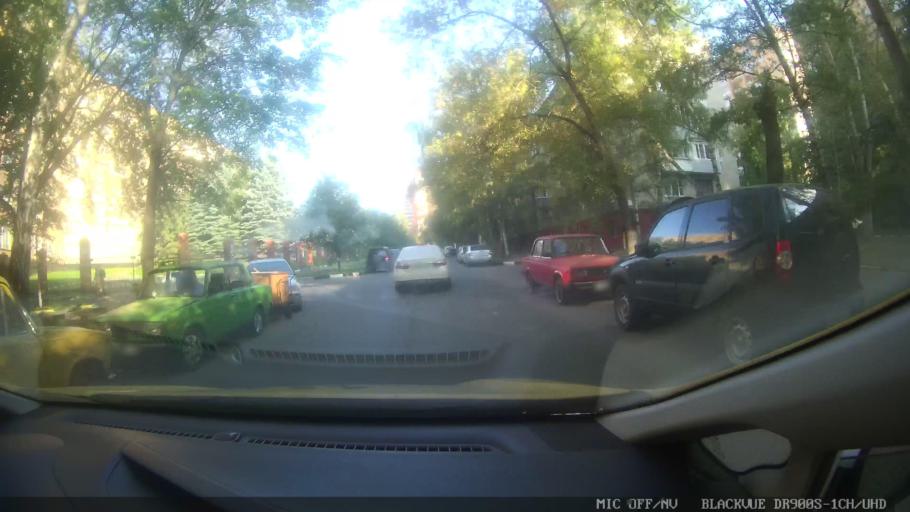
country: RU
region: Moskovskaya
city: Lyubertsy
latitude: 55.6771
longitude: 37.8753
